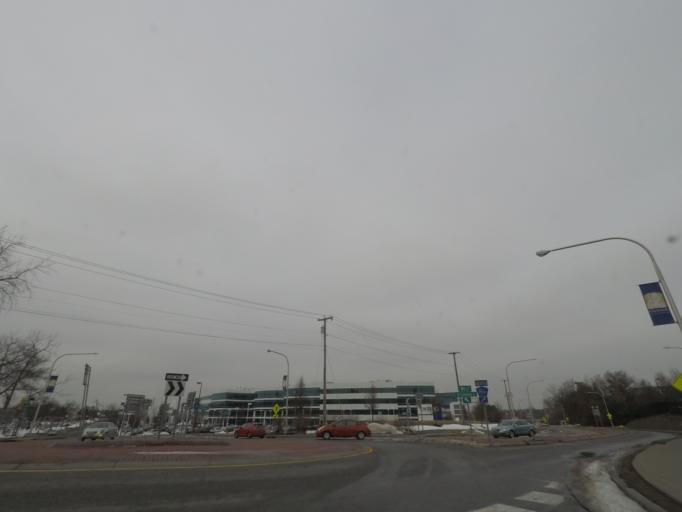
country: US
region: New York
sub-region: Albany County
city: McKownville
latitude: 42.6890
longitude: -73.8309
